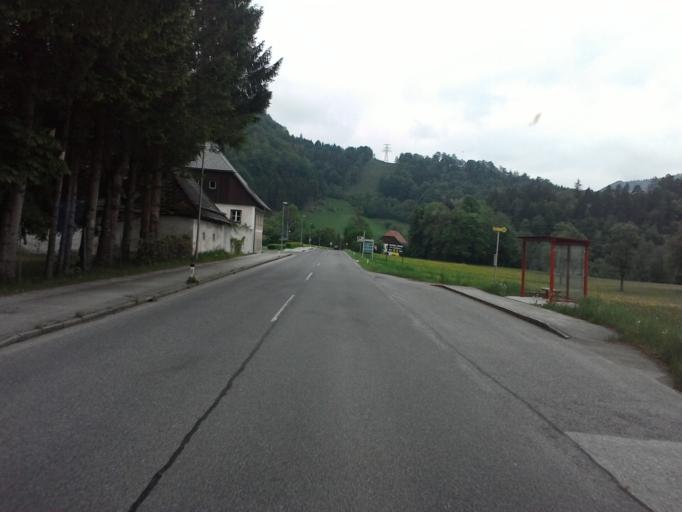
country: AT
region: Styria
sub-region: Politischer Bezirk Liezen
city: Landl
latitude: 47.6573
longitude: 14.7326
